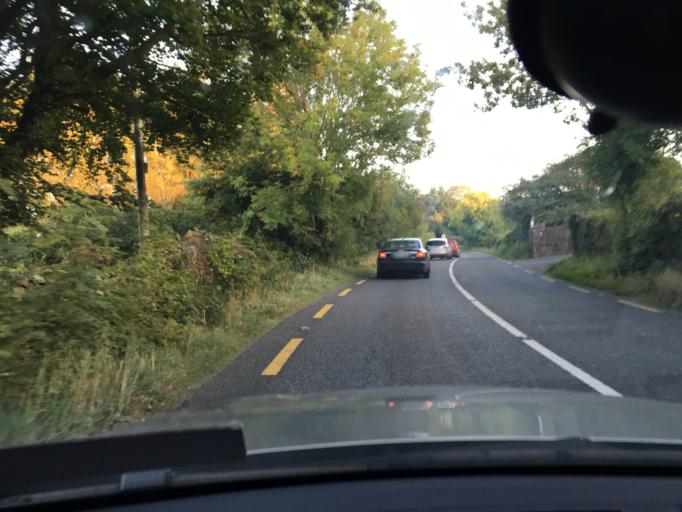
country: IE
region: Connaught
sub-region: County Galway
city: Gaillimh
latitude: 53.3019
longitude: -9.1042
